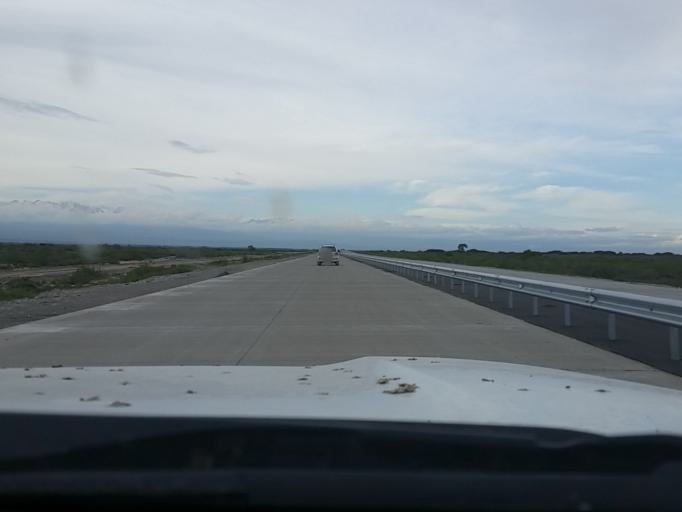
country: KZ
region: Almaty Oblysy
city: Zharkent
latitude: 44.0768
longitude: 80.0407
